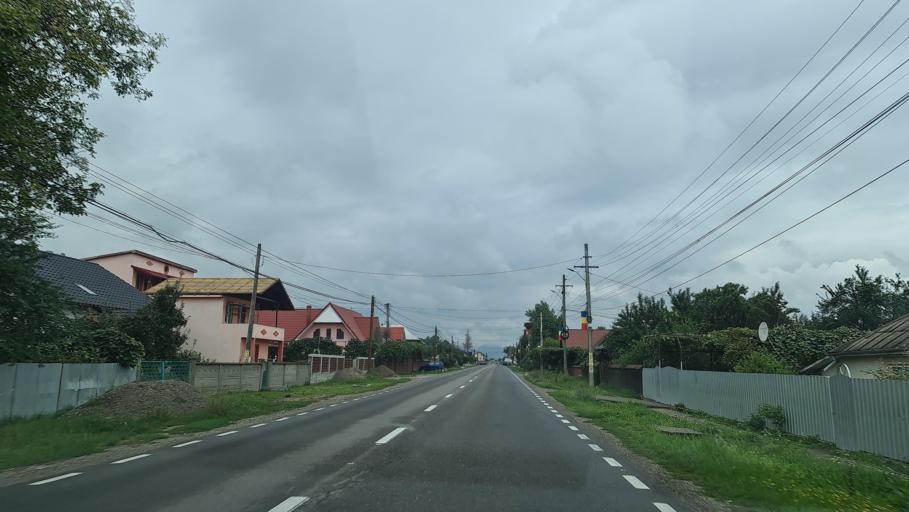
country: RO
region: Neamt
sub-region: Comuna Borlesti
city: Ruseni
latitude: 46.8007
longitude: 26.5339
